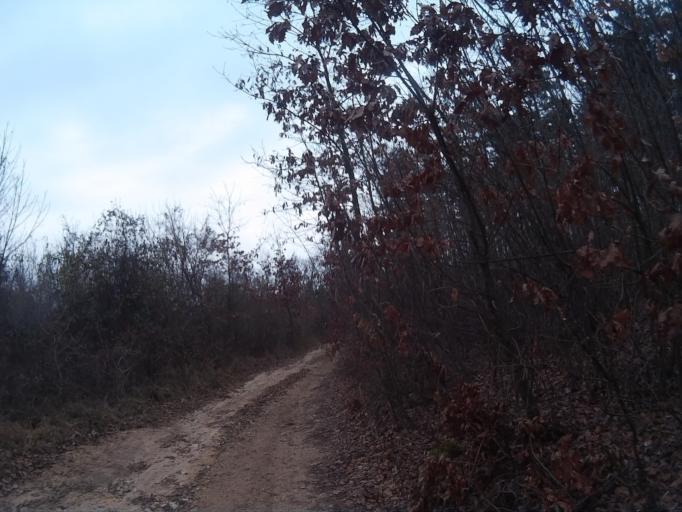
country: HU
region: Veszprem
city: Tapolca
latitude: 46.9821
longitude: 17.4911
